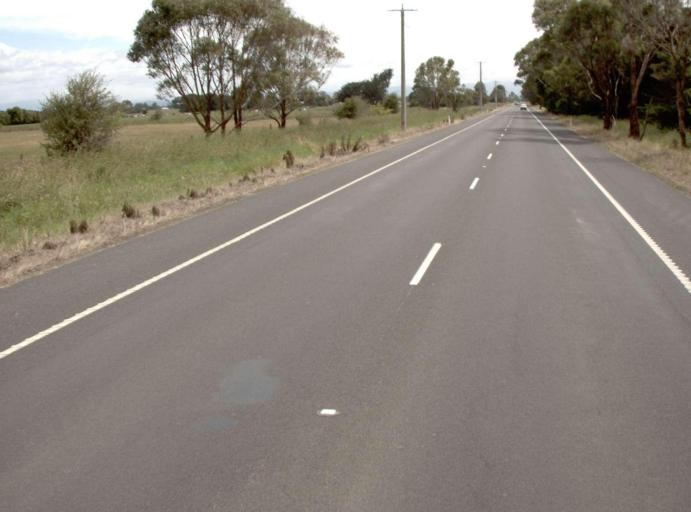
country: AU
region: Victoria
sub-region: Wellington
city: Sale
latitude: -38.0353
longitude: 147.0168
